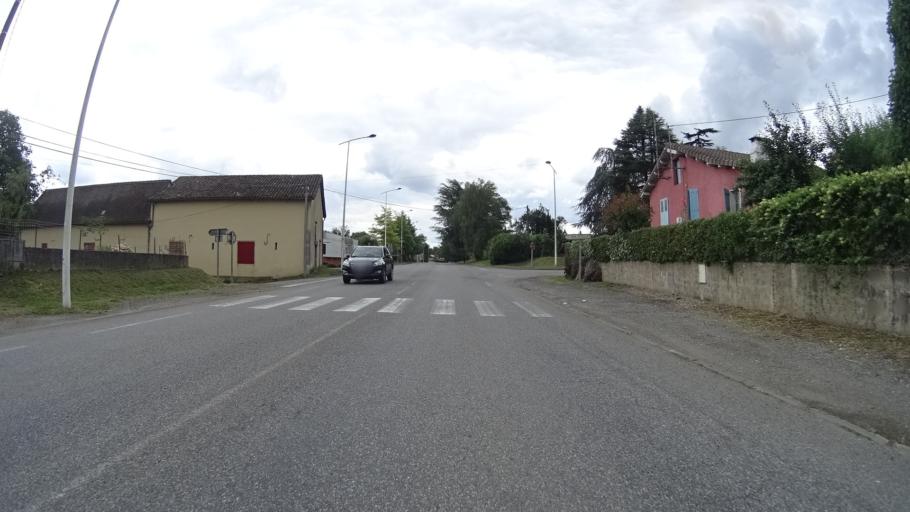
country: FR
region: Aquitaine
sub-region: Departement des Pyrenees-Atlantiques
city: Orthez
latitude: 43.4872
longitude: -0.7594
